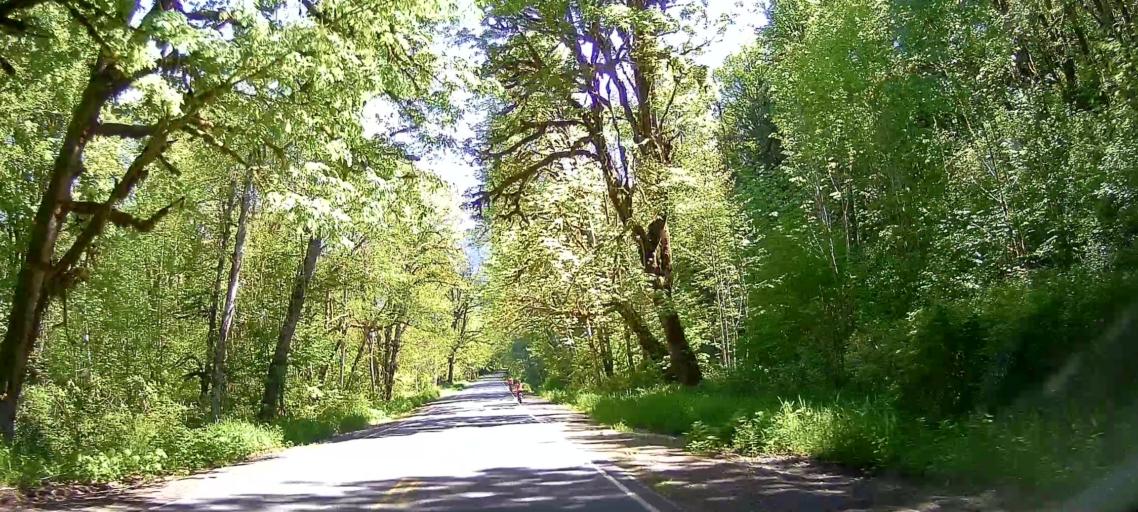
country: US
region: Washington
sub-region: Snohomish County
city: Darrington
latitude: 48.5060
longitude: -121.6928
